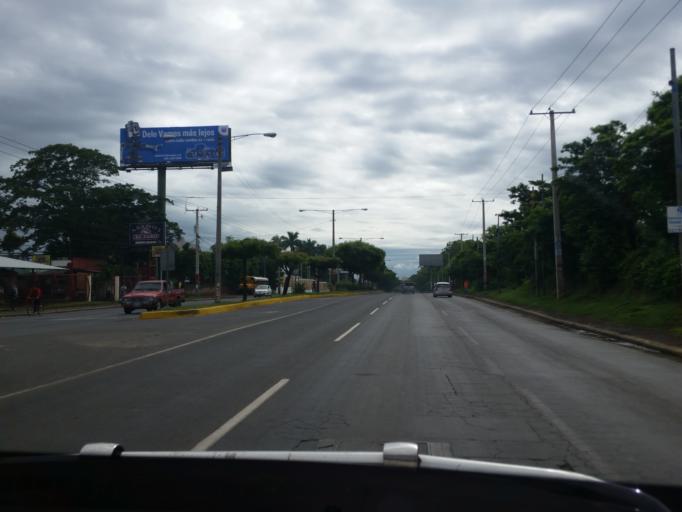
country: NI
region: Managua
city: Managua
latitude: 12.1472
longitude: -86.1879
